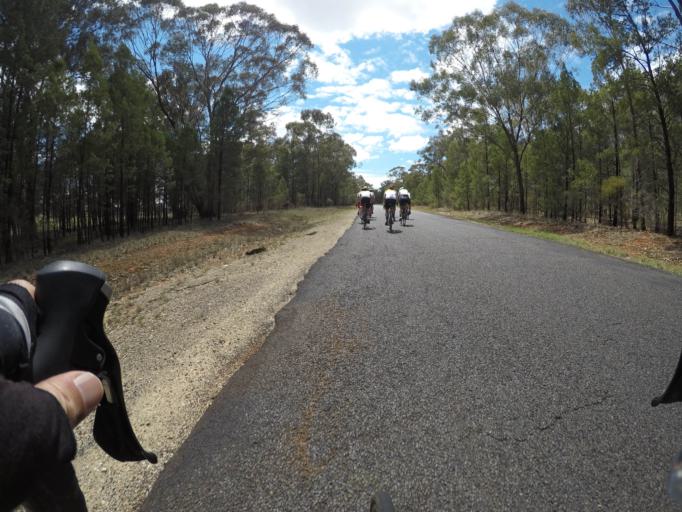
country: AU
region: New South Wales
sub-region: Dubbo Municipality
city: Dubbo
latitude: -32.3805
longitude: 148.5764
